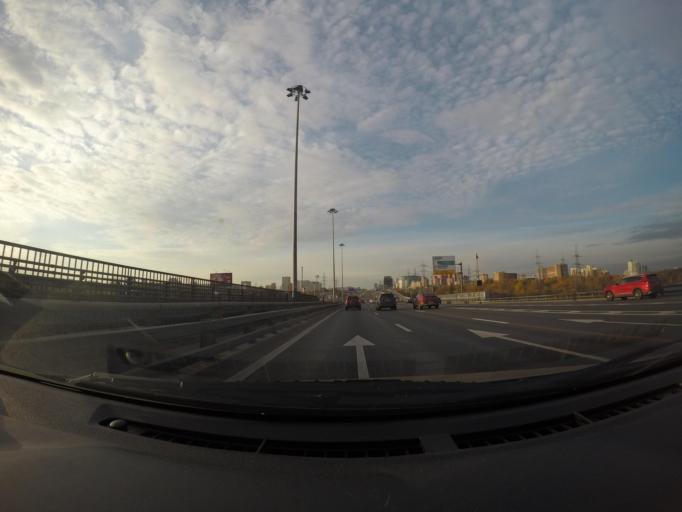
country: RU
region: Moskovskaya
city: Levoberezhnaya
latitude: 55.8738
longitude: 37.4549
